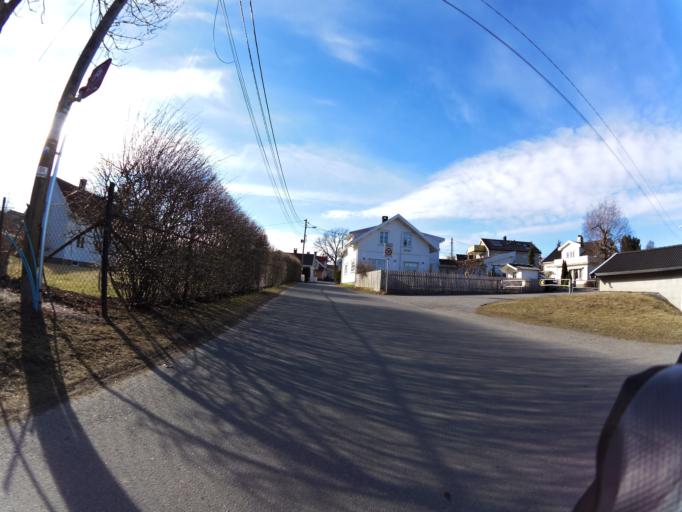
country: NO
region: Ostfold
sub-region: Fredrikstad
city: Fredrikstad
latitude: 59.2148
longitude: 10.9095
